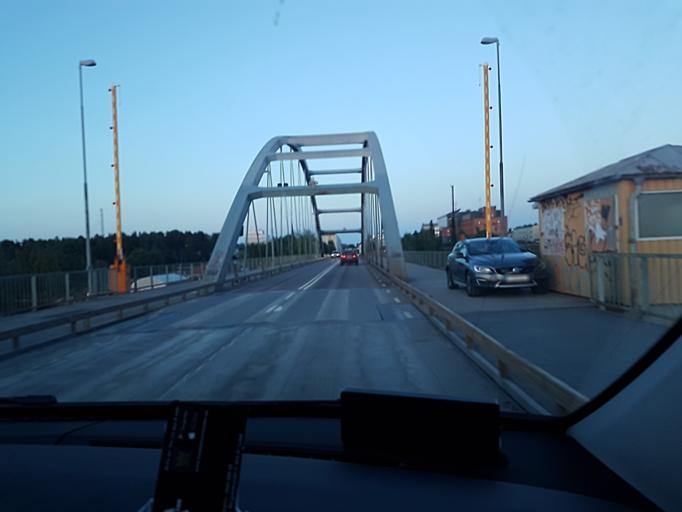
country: SE
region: Norrbotten
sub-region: Lulea Kommun
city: Bergnaset
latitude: 65.5793
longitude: 22.1268
